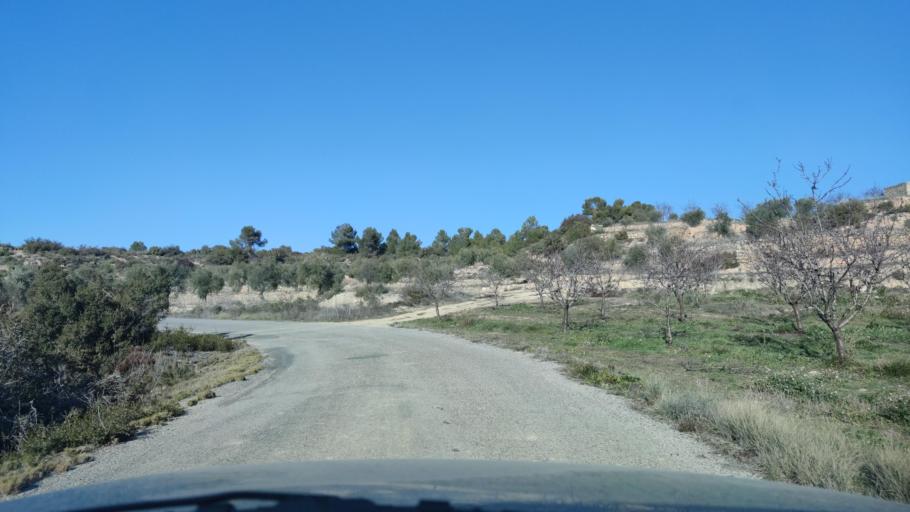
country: ES
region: Catalonia
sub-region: Provincia de Lleida
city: Torrebesses
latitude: 41.3919
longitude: 0.5647
